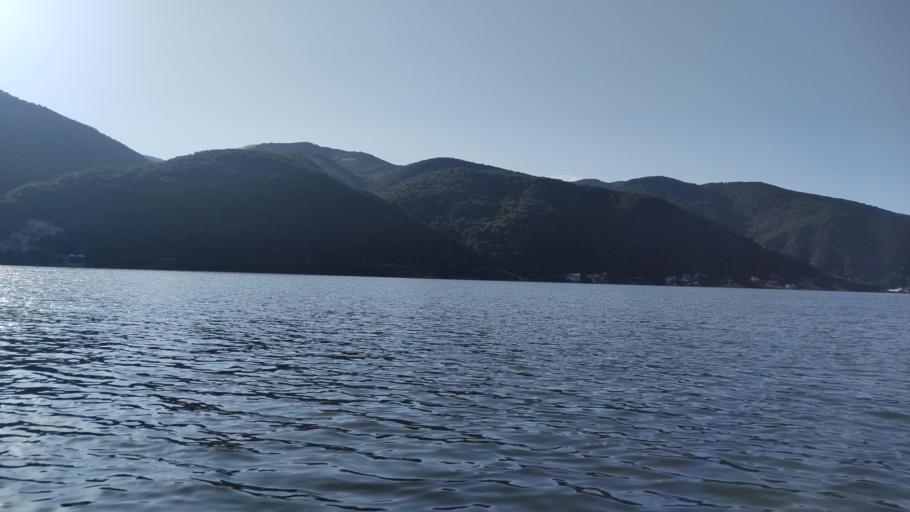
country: RO
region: Mehedinti
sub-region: Comuna Dubova
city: Dubova
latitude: 44.5578
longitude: 22.2317
